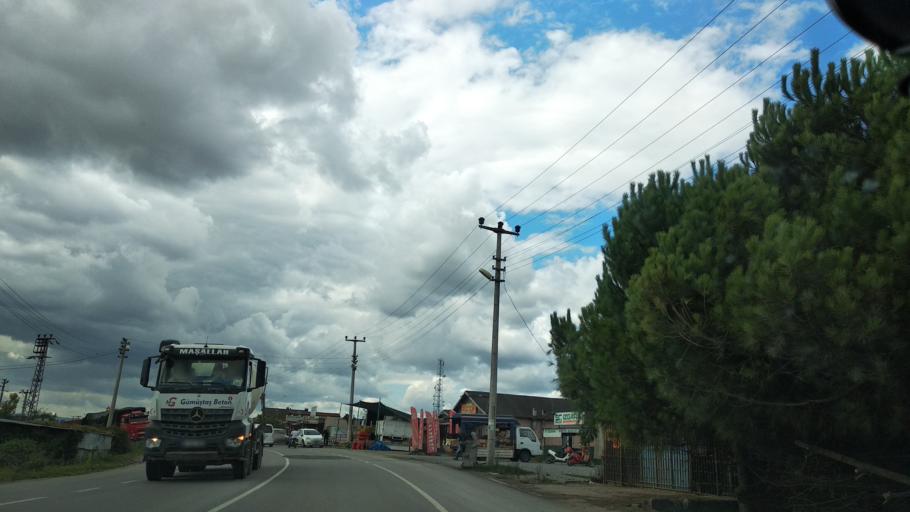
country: TR
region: Sakarya
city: Adapazari
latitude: 40.7968
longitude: 30.4356
